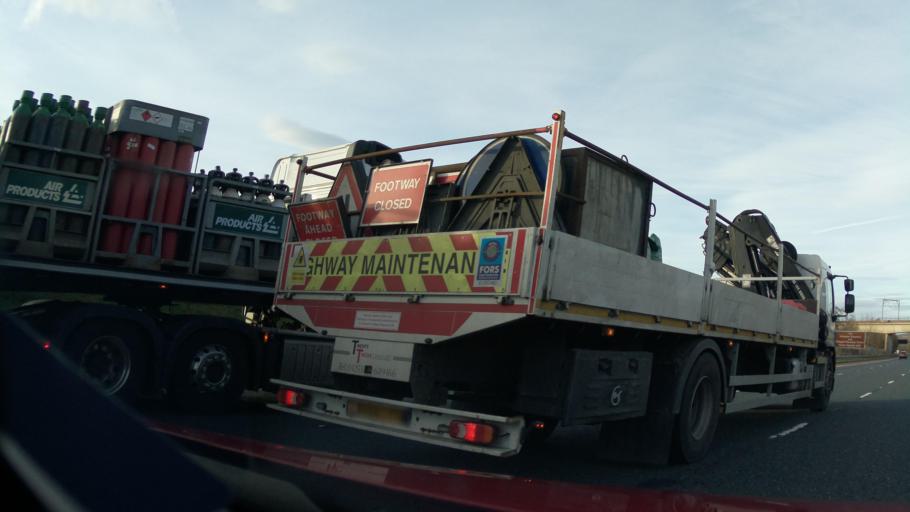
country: GB
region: England
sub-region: Cumbria
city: Penrith
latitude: 54.6327
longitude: -2.7264
